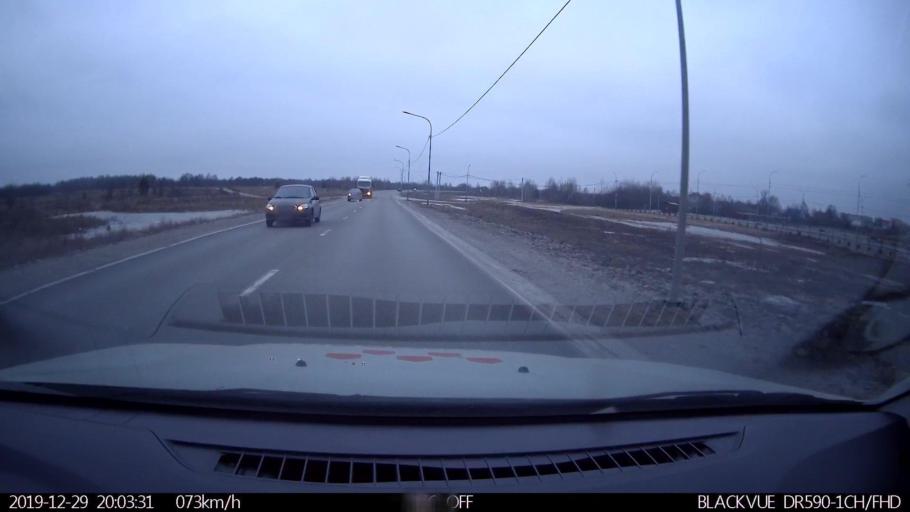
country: RU
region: Nizjnij Novgorod
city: Nizhniy Novgorod
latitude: 56.3744
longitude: 44.0165
